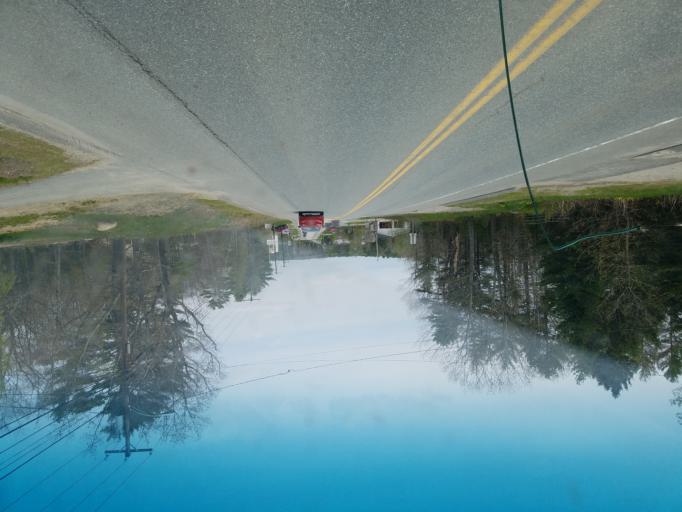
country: US
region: Maine
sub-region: Hancock County
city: Ellsworth
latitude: 44.5668
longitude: -68.4491
